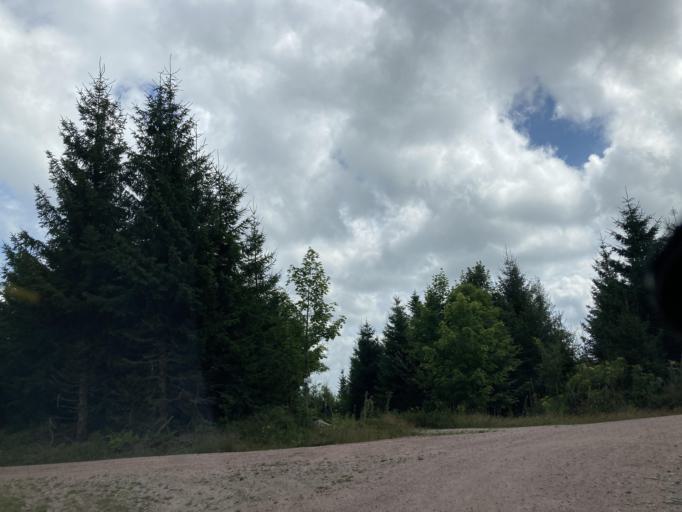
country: DE
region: Baden-Wuerttemberg
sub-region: Freiburg Region
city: Schonach im Schwarzwald
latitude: 48.1552
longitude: 8.1415
